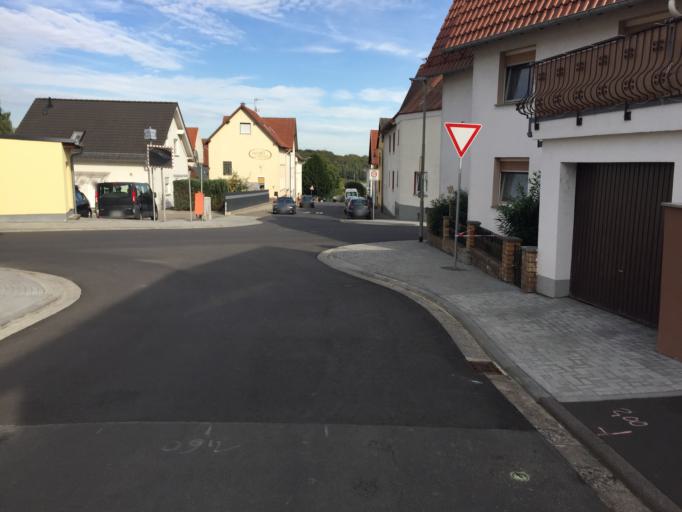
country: DE
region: Hesse
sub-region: Regierungsbezirk Giessen
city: Langgons
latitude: 50.5115
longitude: 8.7286
